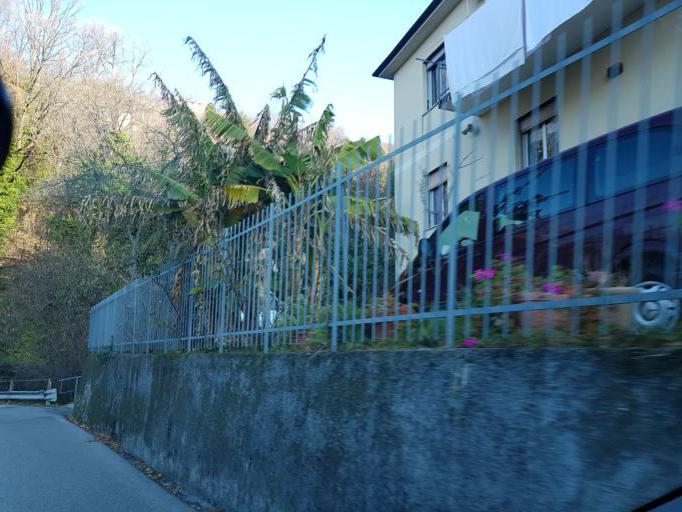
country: IT
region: Liguria
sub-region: Provincia di Genova
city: Manesseno
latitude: 44.4581
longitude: 8.9211
